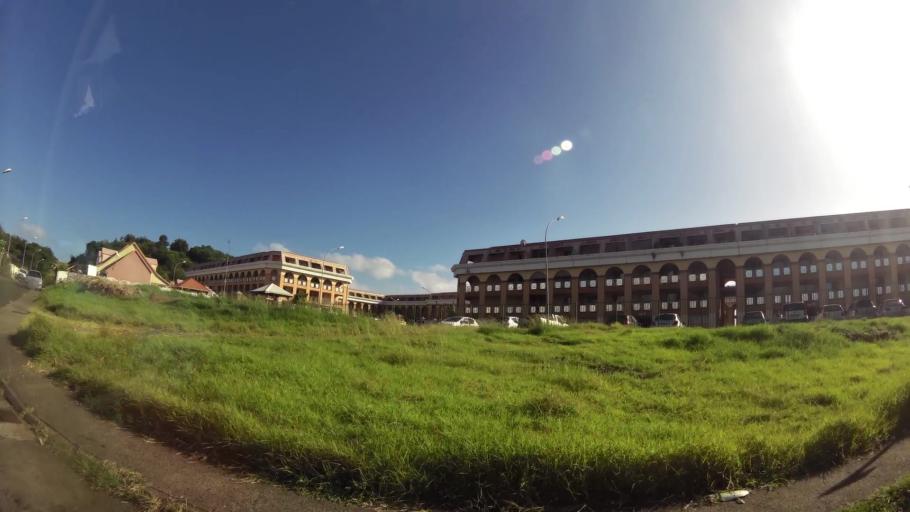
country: MQ
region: Martinique
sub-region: Martinique
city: Le Francois
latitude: 14.6215
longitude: -60.9017
